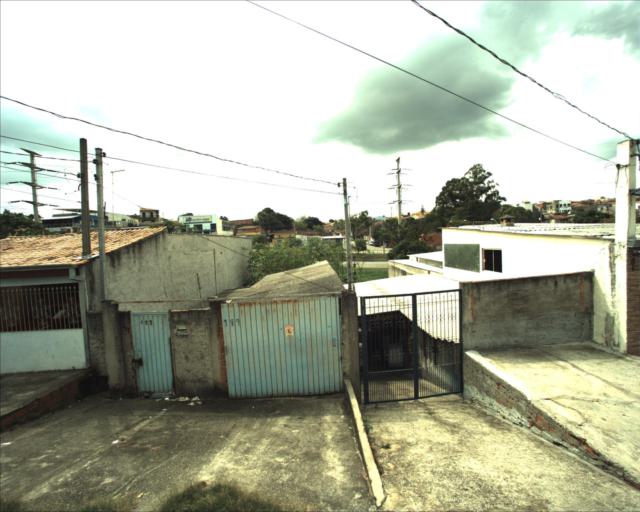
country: BR
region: Sao Paulo
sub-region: Sorocaba
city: Sorocaba
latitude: -23.4553
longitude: -47.4805
